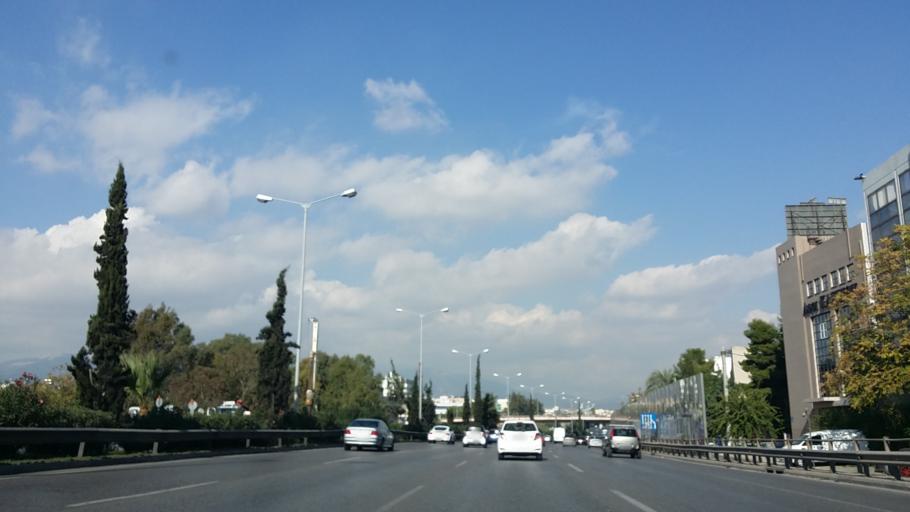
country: GR
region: Attica
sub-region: Nomarchia Athinas
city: Nea Chalkidona
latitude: 38.0237
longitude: 23.7257
